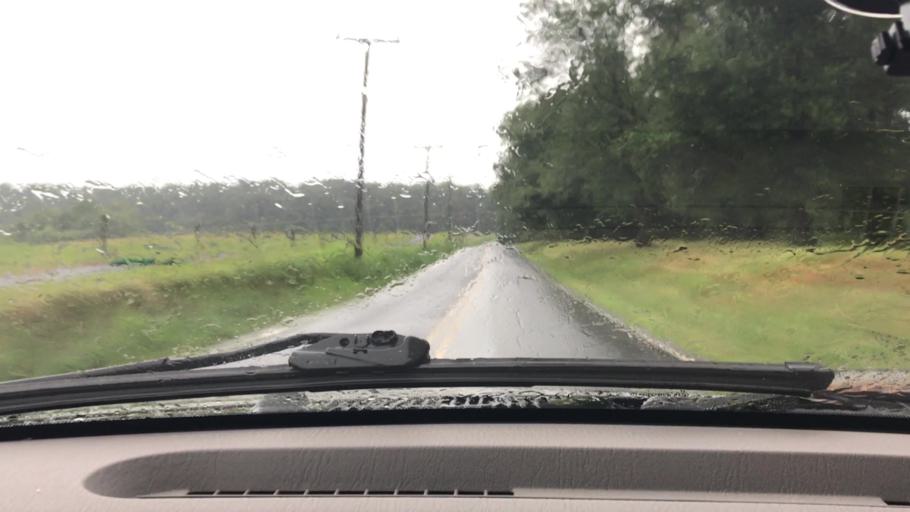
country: US
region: Pennsylvania
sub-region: Lancaster County
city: Elizabethtown
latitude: 40.1334
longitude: -76.6167
